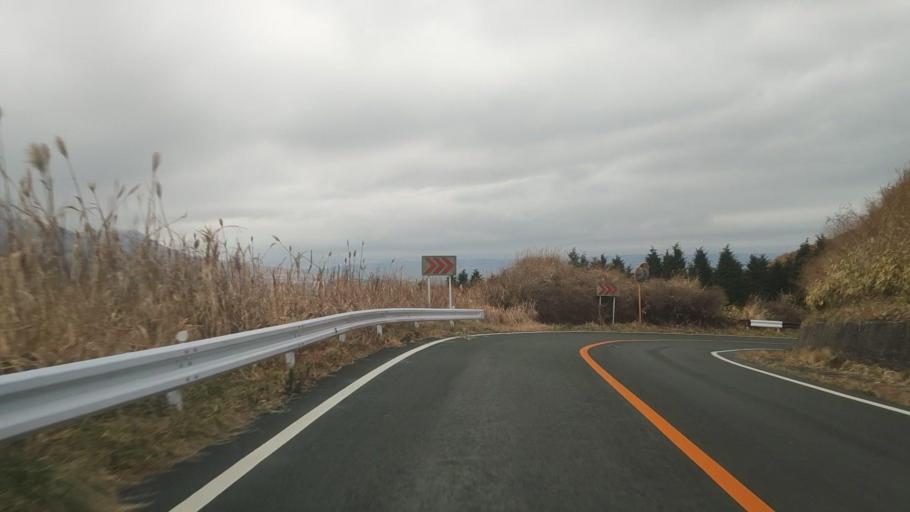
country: JP
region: Kumamoto
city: Aso
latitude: 32.9041
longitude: 131.1474
